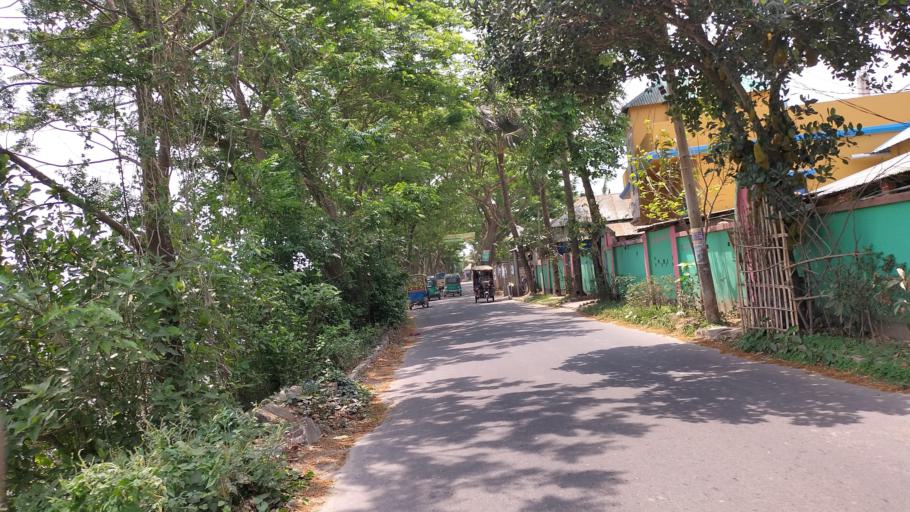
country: BD
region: Dhaka
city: Azimpur
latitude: 23.7410
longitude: 90.2491
